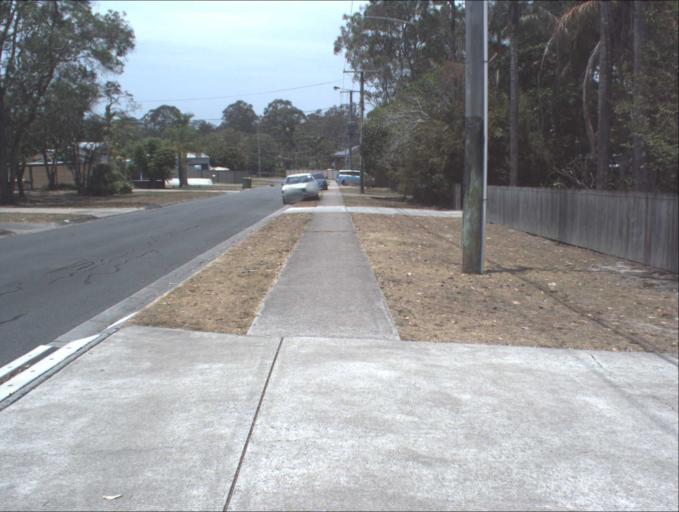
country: AU
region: Queensland
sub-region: Logan
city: Slacks Creek
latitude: -27.6684
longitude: 153.1838
